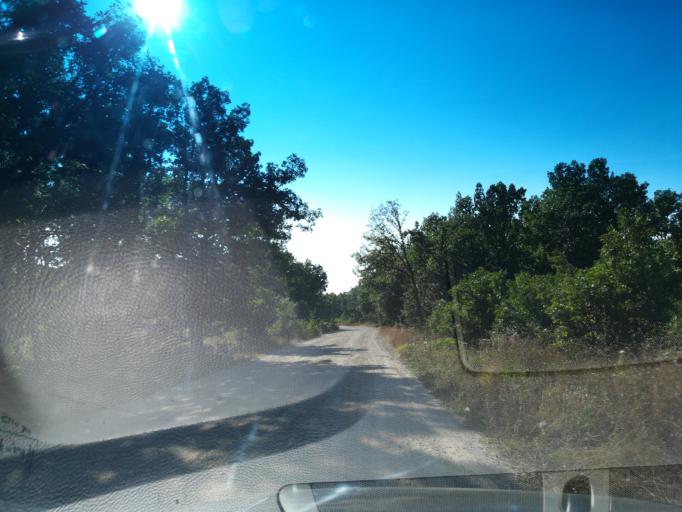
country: BG
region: Khaskovo
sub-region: Obshtina Mineralni Bani
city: Mineralni Bani
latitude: 41.9717
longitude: 25.3322
